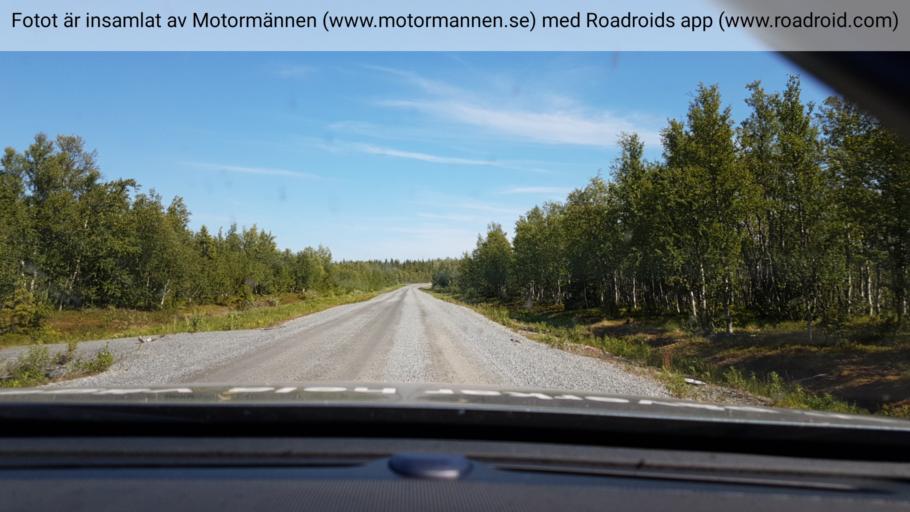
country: SE
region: Vaesterbotten
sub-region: Vilhelmina Kommun
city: Sjoberg
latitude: 64.7699
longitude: 15.9129
